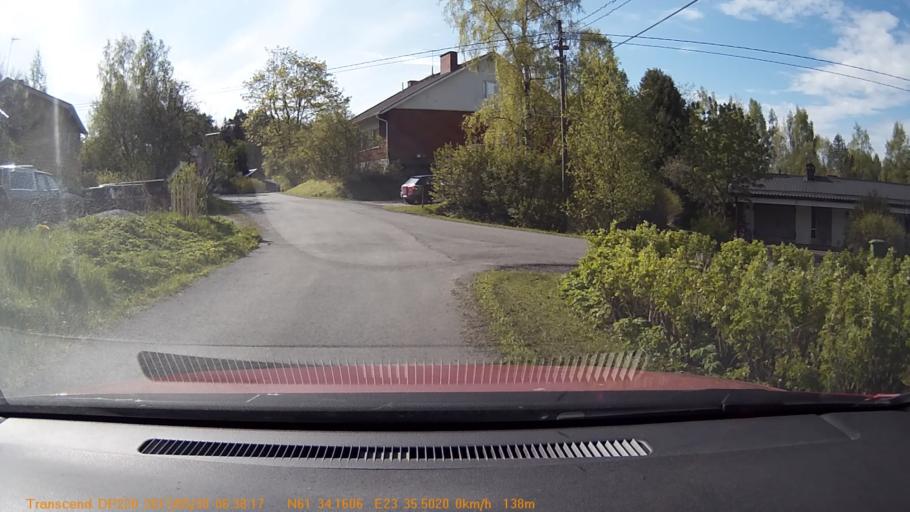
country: FI
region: Pirkanmaa
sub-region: Tampere
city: Yloejaervi
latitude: 61.5693
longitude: 23.5917
